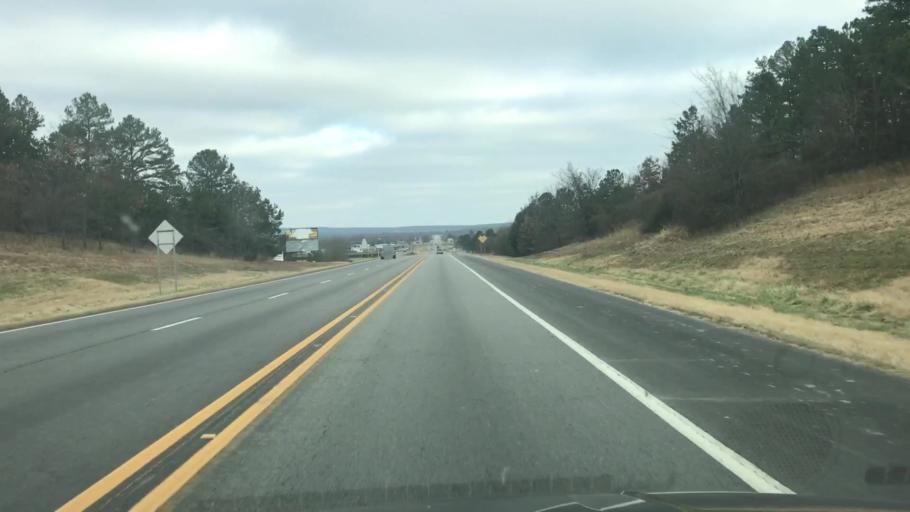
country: US
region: Arkansas
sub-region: Scott County
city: Waldron
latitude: 34.8887
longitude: -94.1077
